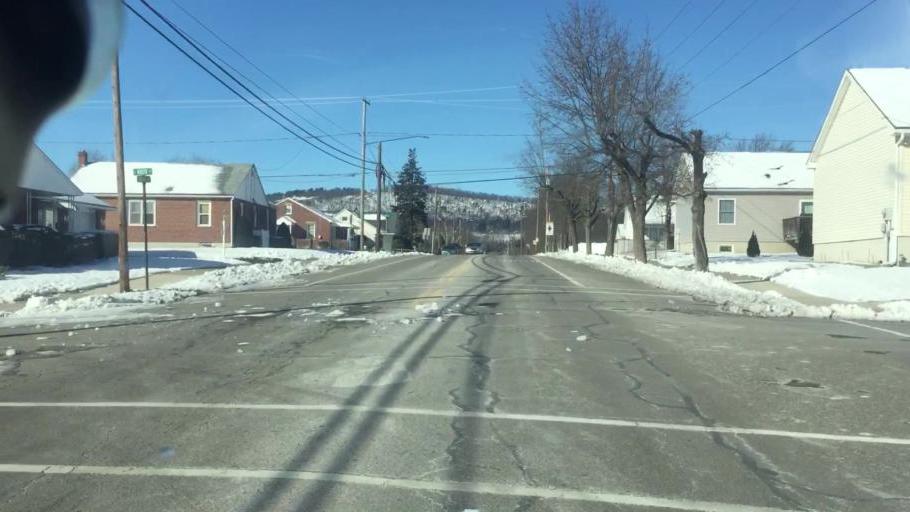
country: US
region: Pennsylvania
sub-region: Luzerne County
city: East Berwick
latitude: 41.0642
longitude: -76.2288
